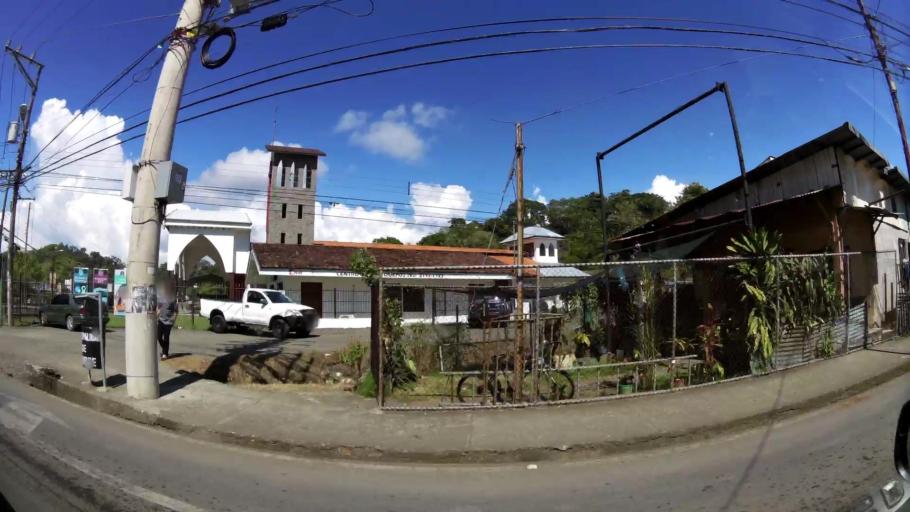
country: CR
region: Puntarenas
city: Quepos
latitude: 9.4294
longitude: -84.1600
